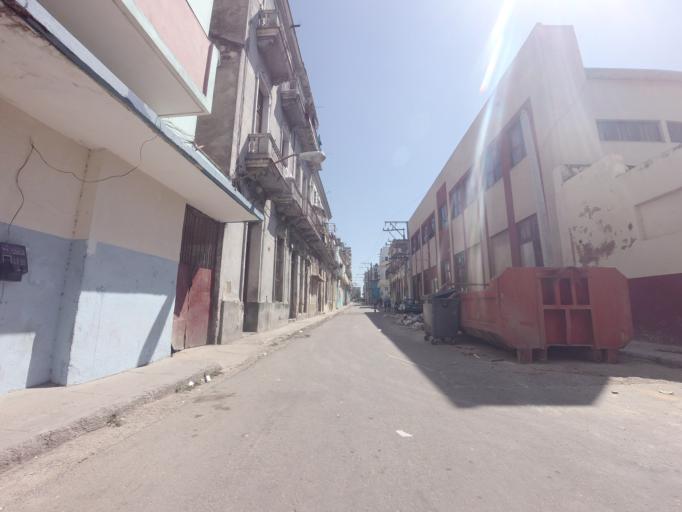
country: CU
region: La Habana
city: Centro Habana
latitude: 23.1344
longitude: -82.3707
